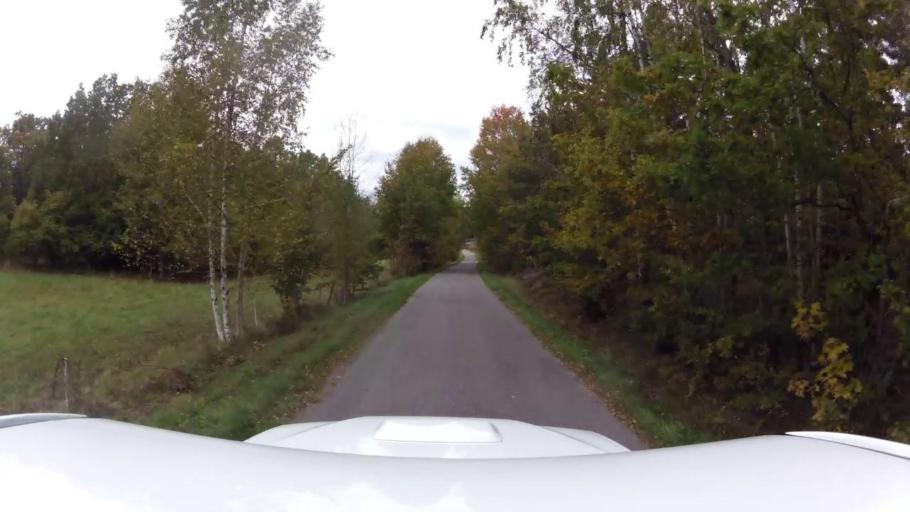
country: SE
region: OEstergoetland
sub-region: Kinda Kommun
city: Rimforsa
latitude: 58.1930
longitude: 15.6171
